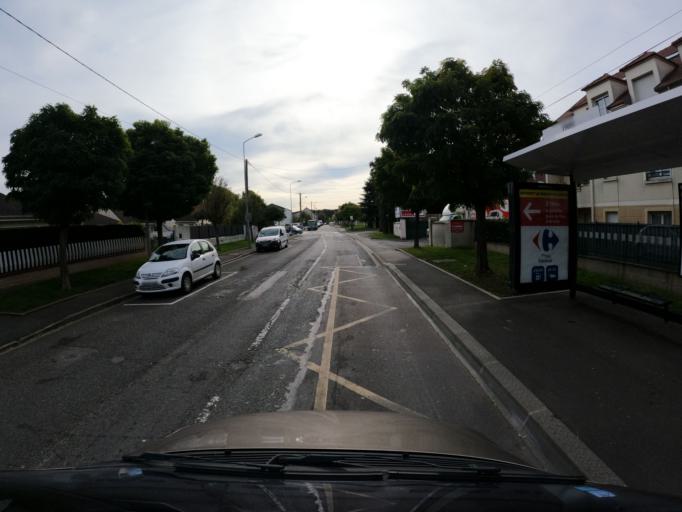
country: FR
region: Ile-de-France
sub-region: Departement du Val-de-Marne
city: La Queue-en-Brie
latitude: 48.7782
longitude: 2.5987
